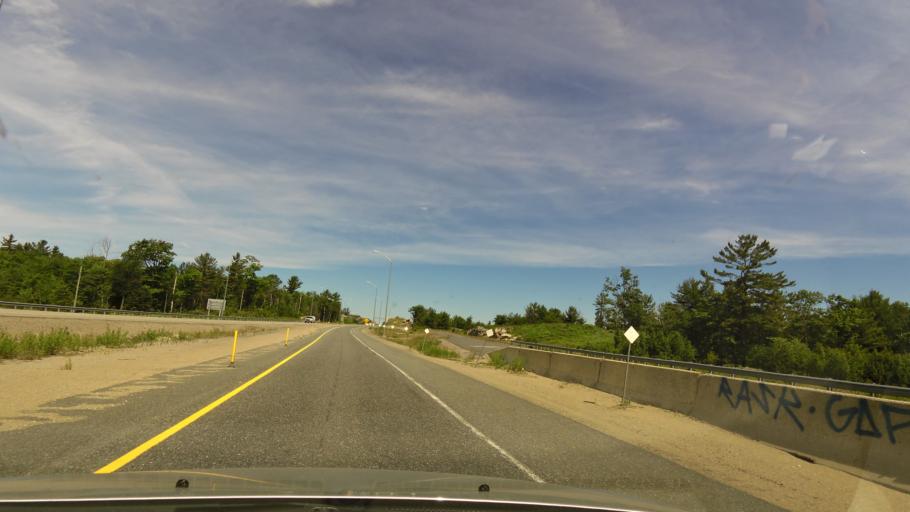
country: CA
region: Ontario
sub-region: Parry Sound District
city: Parry Sound
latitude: 45.4518
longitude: -80.1456
